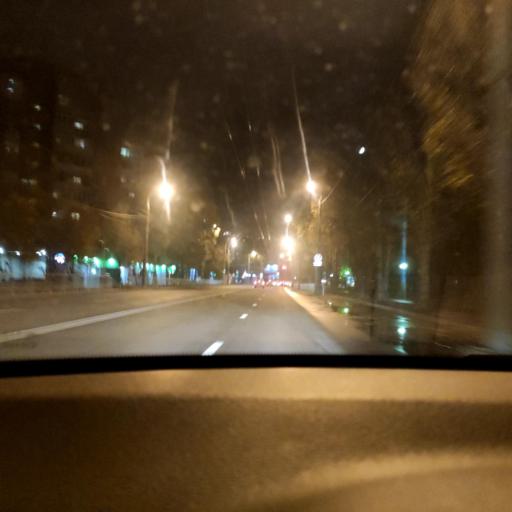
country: RU
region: Samara
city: Samara
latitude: 53.2407
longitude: 50.2277
